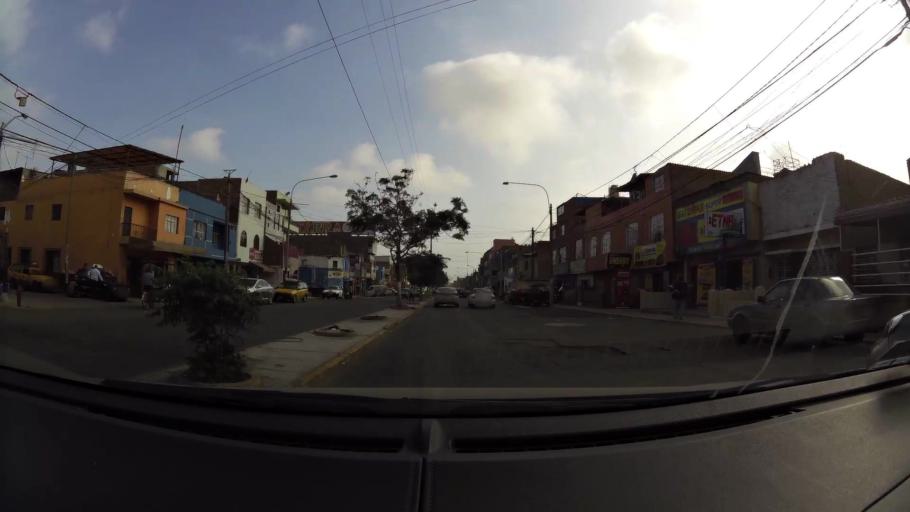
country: PE
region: La Libertad
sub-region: Provincia de Trujillo
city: Trujillo
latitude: -8.1013
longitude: -79.0160
